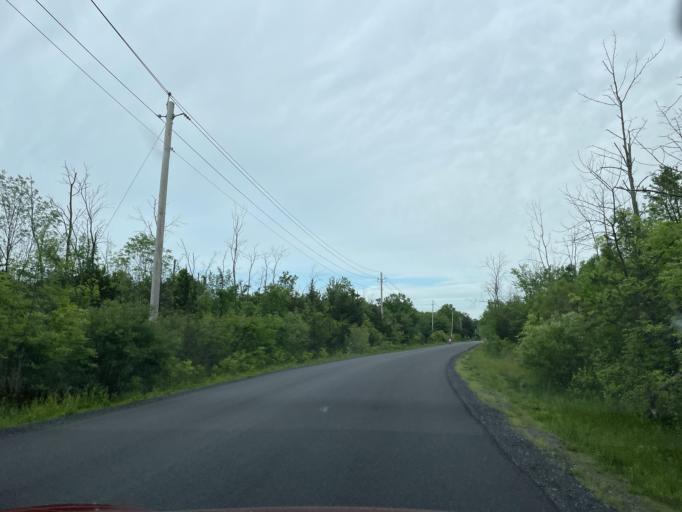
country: US
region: New York
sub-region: Ulster County
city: Saugerties
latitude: 42.0985
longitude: -73.9506
